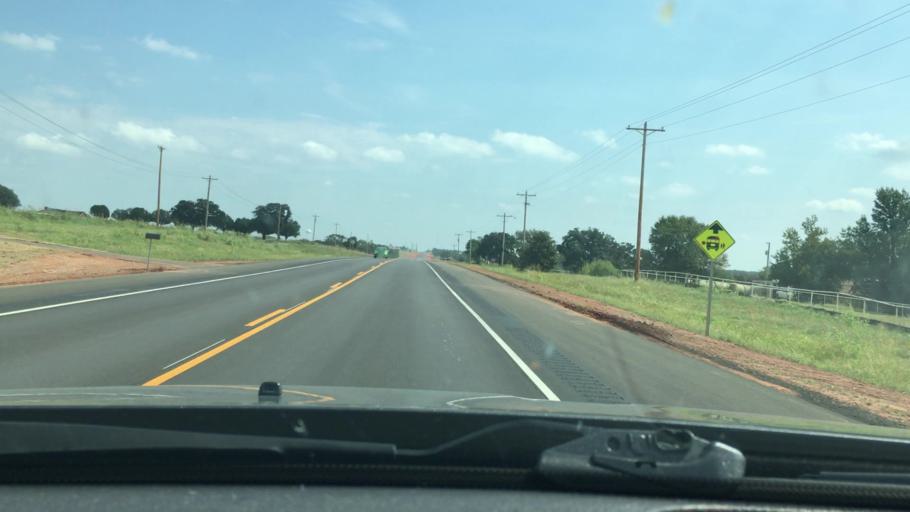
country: US
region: Oklahoma
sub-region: Cleveland County
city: Lexington
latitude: 35.0149
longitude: -97.2464
